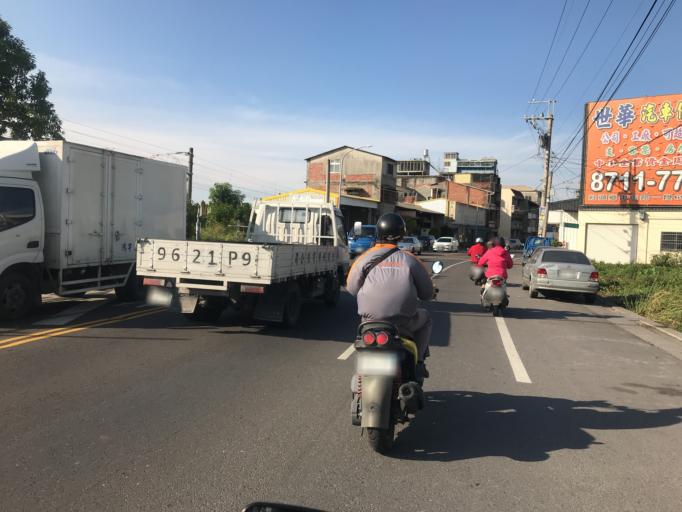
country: TW
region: Taiwan
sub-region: Nantou
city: Nantou
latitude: 23.8687
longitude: 120.5876
